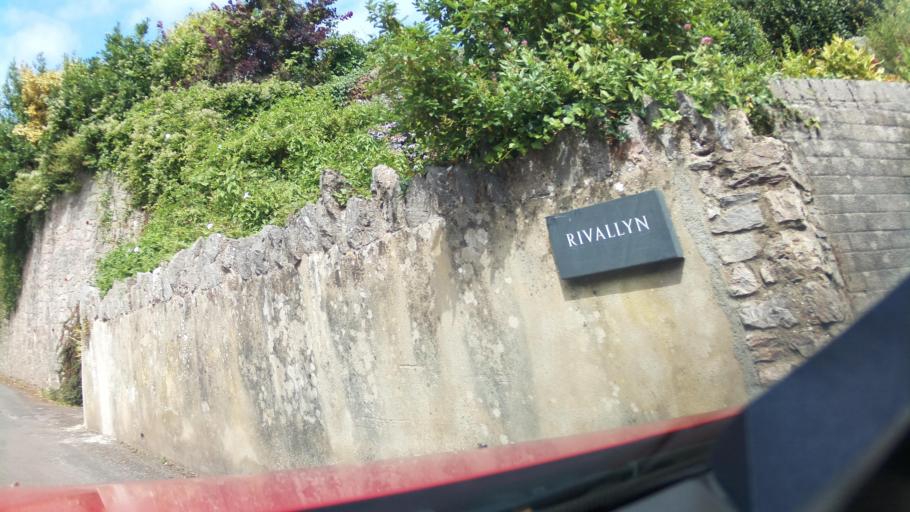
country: GB
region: England
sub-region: Devon
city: Marldon
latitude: 50.4054
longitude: -3.6222
